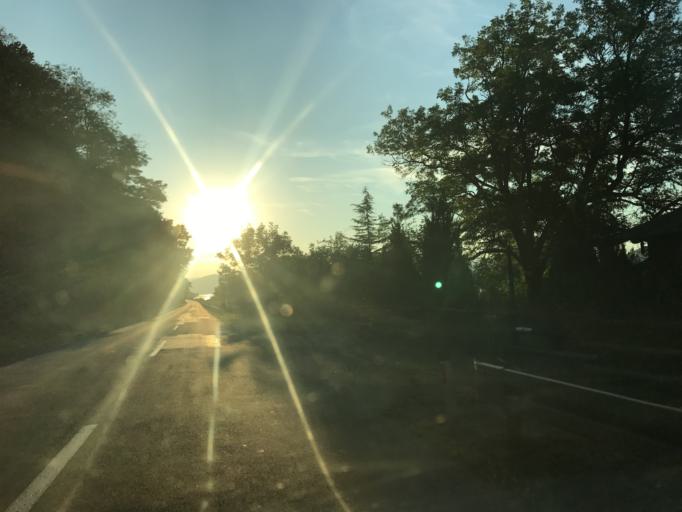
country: RO
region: Caras-Severin
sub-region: Comuna Berzasca
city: Liubcova
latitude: 44.6415
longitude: 21.8946
